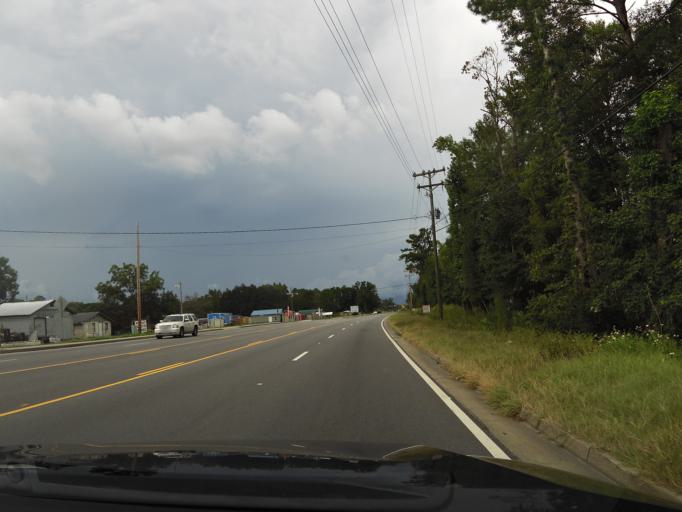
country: US
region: Georgia
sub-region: Glynn County
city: Dock Junction
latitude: 31.2567
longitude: -81.5567
